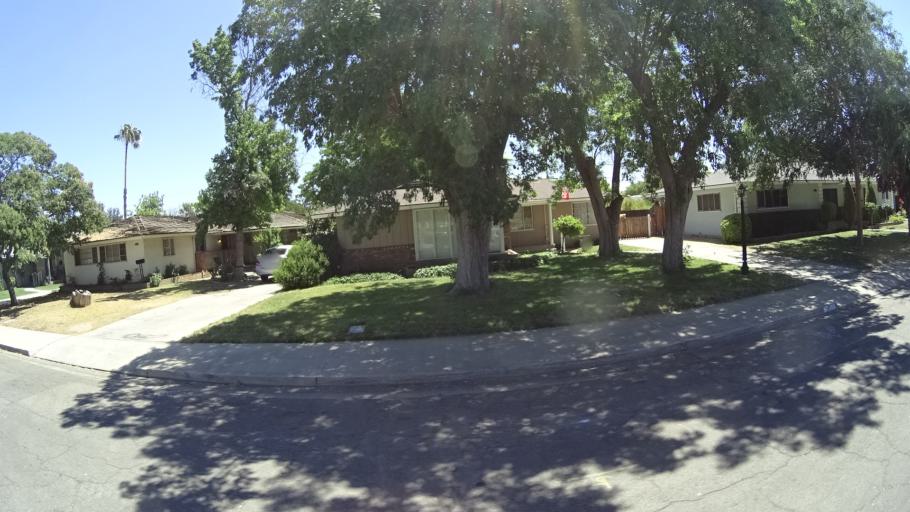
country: US
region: California
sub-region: Fresno County
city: Fresno
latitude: 36.7747
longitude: -119.8154
